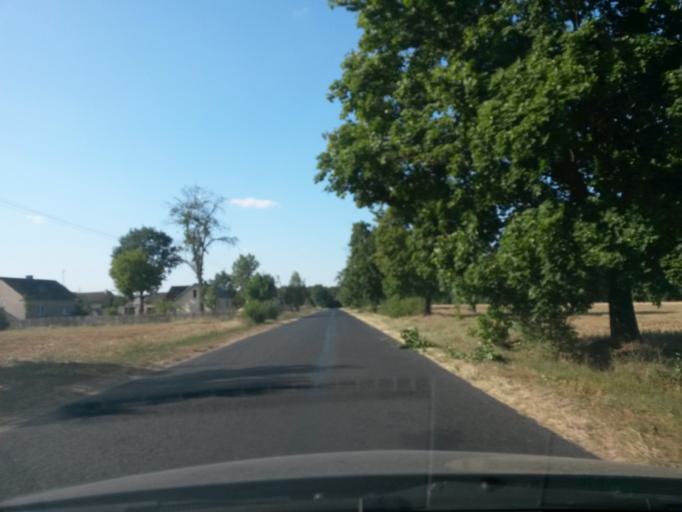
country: PL
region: Kujawsko-Pomorskie
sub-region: Powiat rypinski
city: Skrwilno
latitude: 52.9881
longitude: 19.6287
